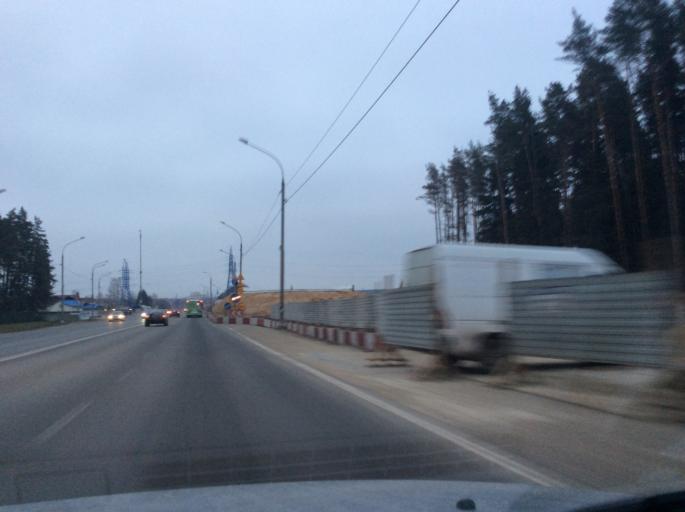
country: RU
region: Moskovskaya
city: Vatutinki
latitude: 55.4841
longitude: 37.3220
